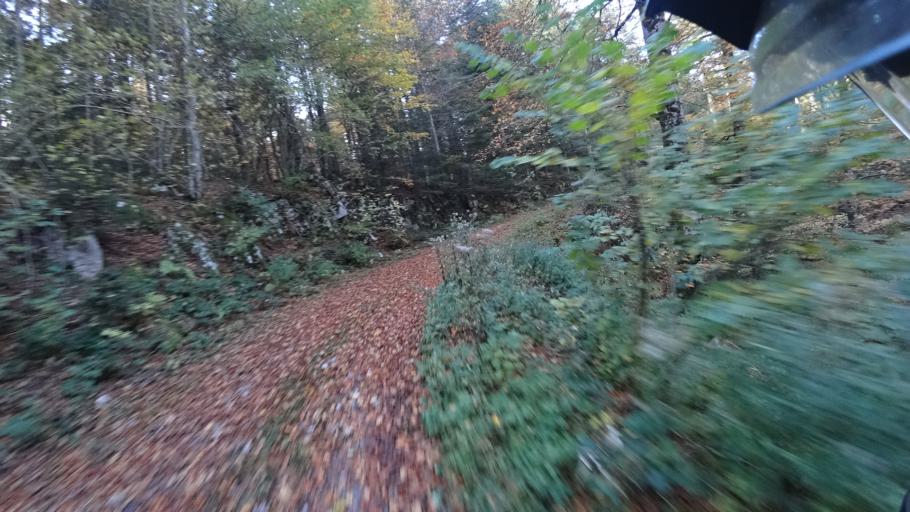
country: HR
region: Karlovacka
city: Plaski
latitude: 45.0430
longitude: 15.3328
